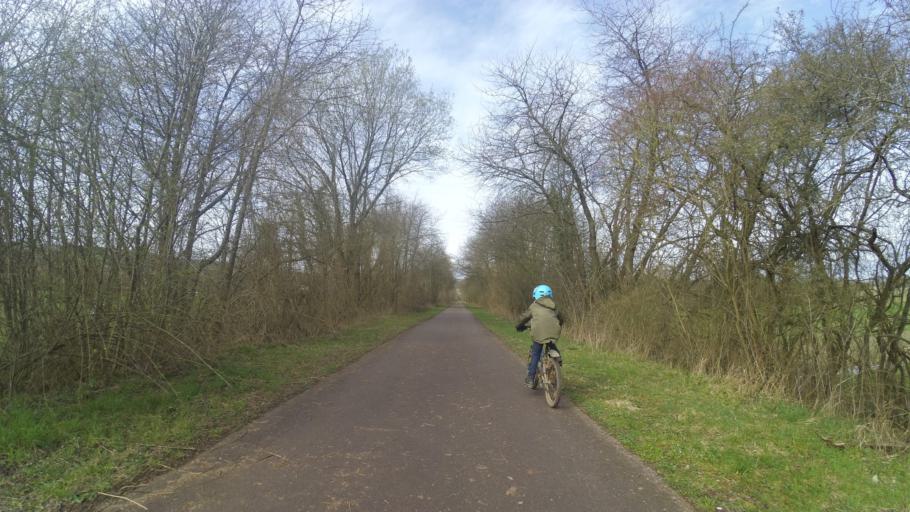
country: FR
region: Lorraine
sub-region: Departement de la Moselle
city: Bliesbruck
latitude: 49.1249
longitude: 7.1853
